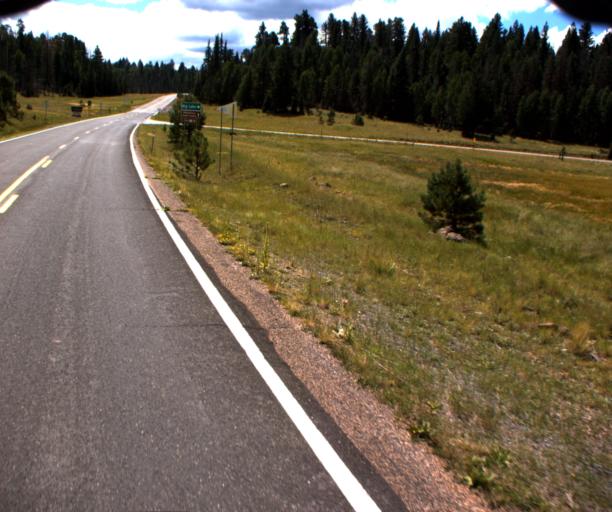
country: US
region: Arizona
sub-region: Apache County
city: Eagar
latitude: 33.8823
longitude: -109.3992
